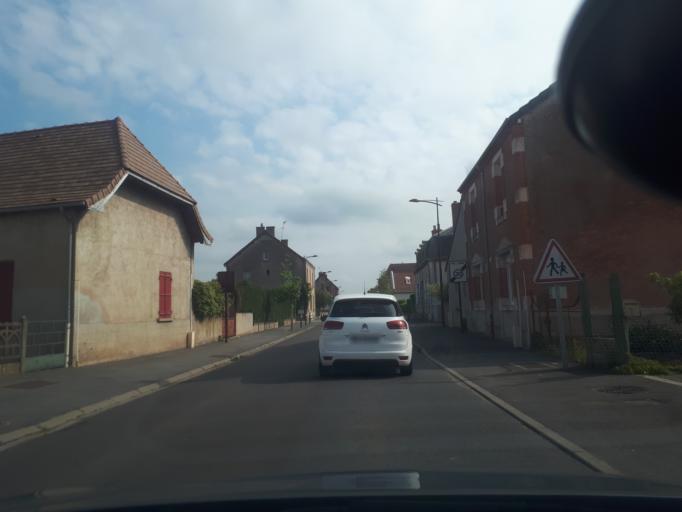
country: FR
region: Auvergne
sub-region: Departement de l'Allier
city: Dompierre-sur-Besbre
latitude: 46.4469
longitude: 3.6306
